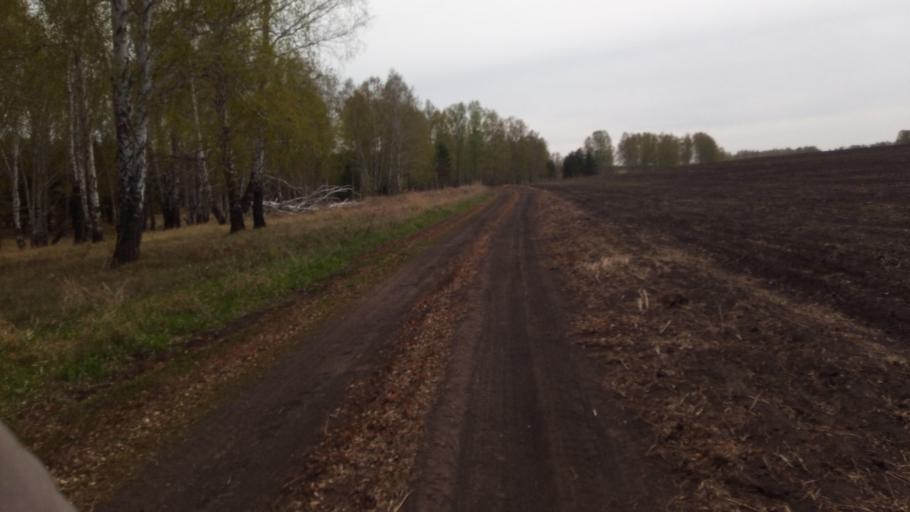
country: RU
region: Chelyabinsk
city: Timiryazevskiy
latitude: 55.0189
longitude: 60.8539
